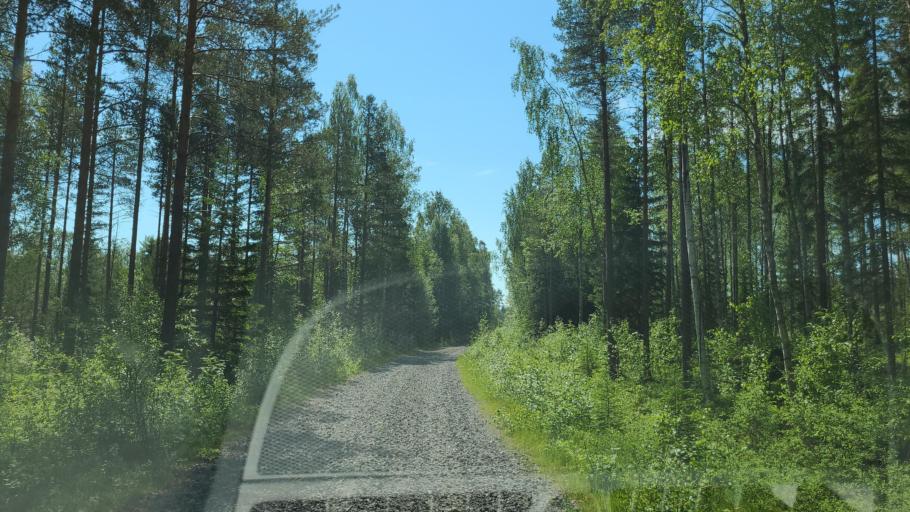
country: SE
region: Vaesterbotten
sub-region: Robertsfors Kommun
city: Robertsfors
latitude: 64.0951
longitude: 20.8348
